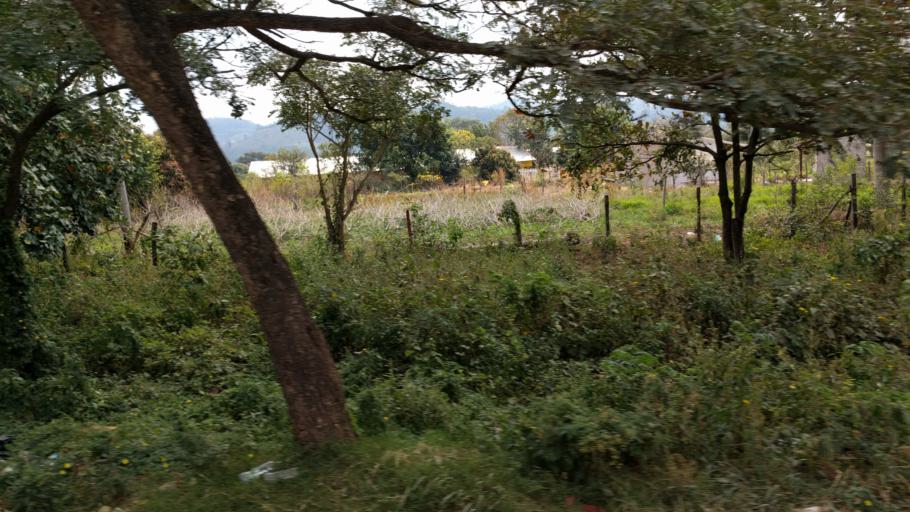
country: BO
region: Santa Cruz
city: Limoncito
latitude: -18.0387
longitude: -63.4101
